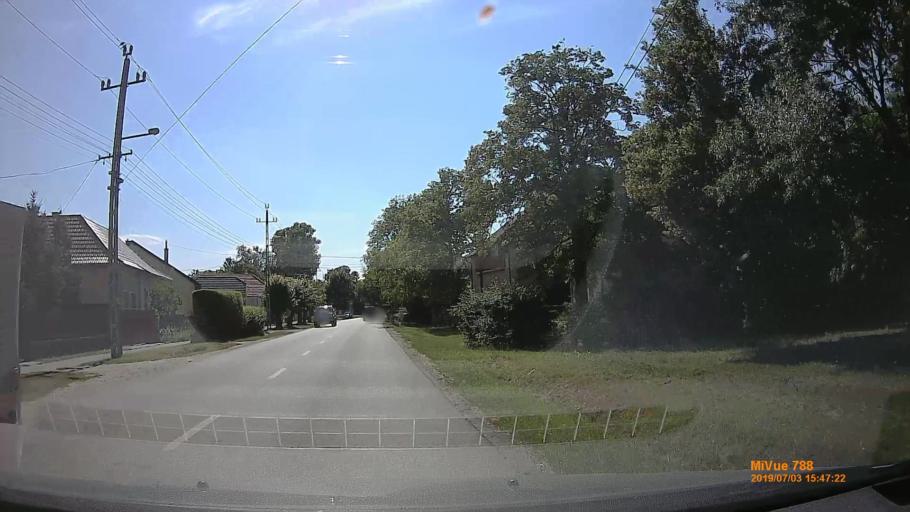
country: HU
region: Gyor-Moson-Sopron
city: Toltestava
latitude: 47.6924
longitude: 17.7443
